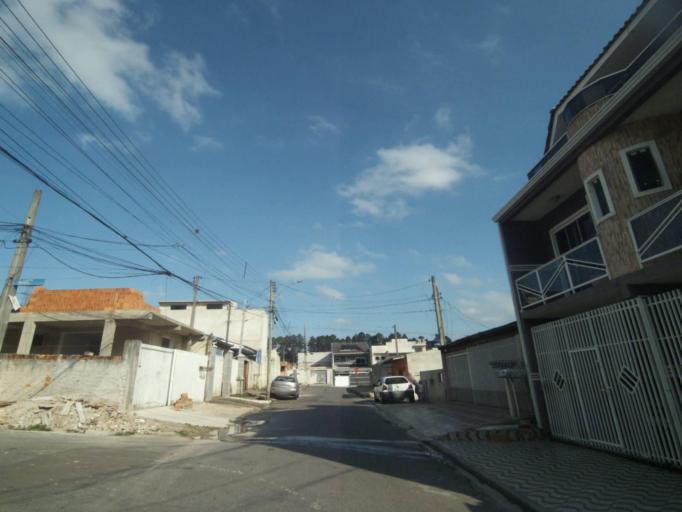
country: BR
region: Parana
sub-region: Araucaria
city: Araucaria
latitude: -25.5339
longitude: -49.3329
